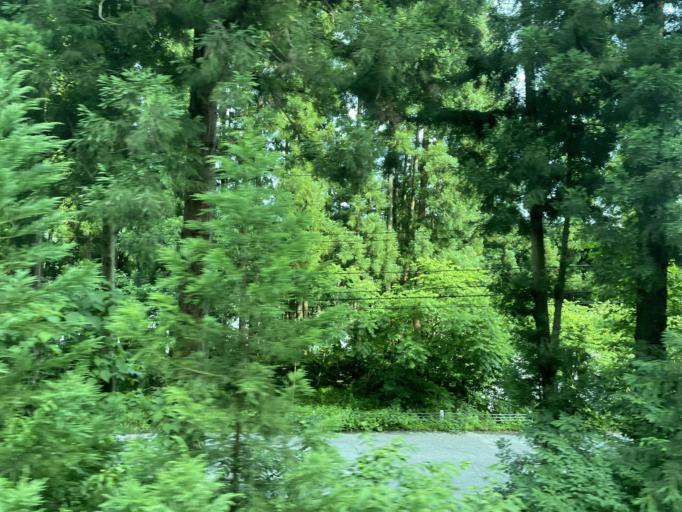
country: JP
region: Niigata
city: Suibara
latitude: 37.6941
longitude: 139.4754
